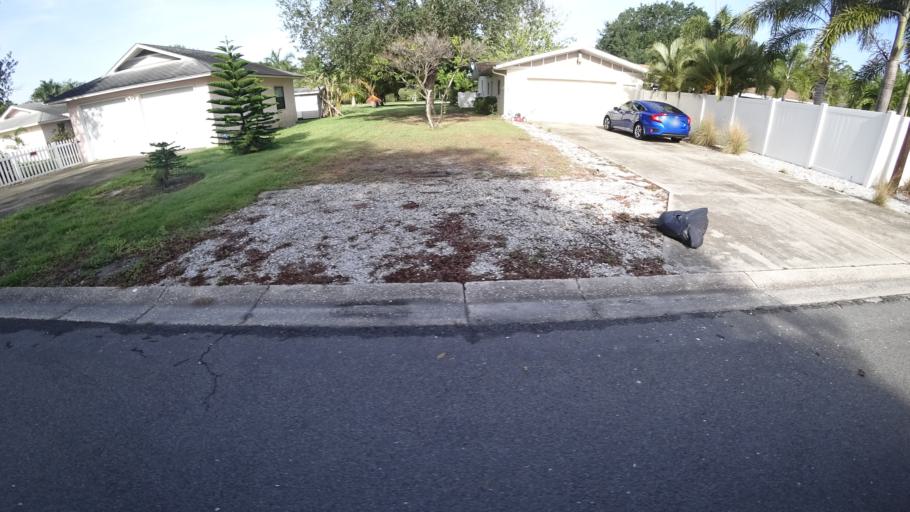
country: US
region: Florida
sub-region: Manatee County
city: West Bradenton
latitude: 27.5043
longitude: -82.6236
